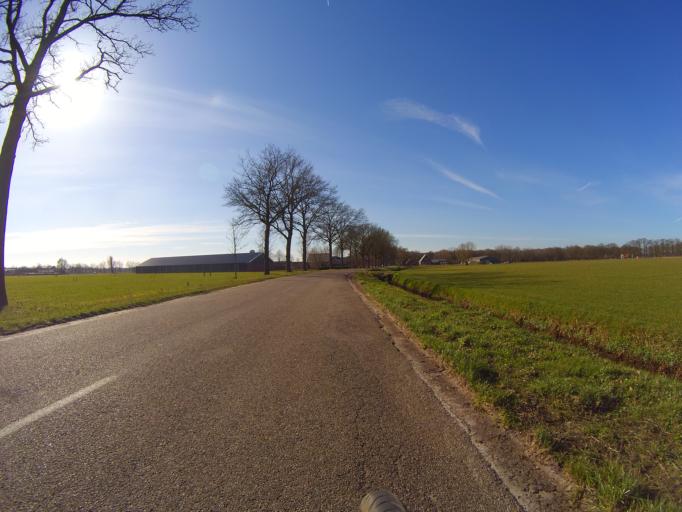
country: NL
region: Utrecht
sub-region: Gemeente Utrechtse Heuvelrug
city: Overberg
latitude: 52.0570
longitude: 5.4962
